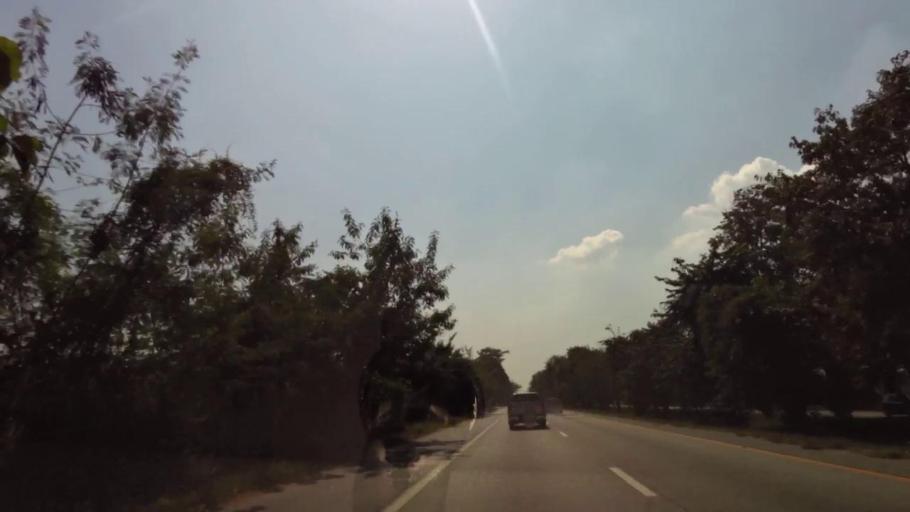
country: TH
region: Phichit
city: Wachira Barami
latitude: 16.5591
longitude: 100.1480
